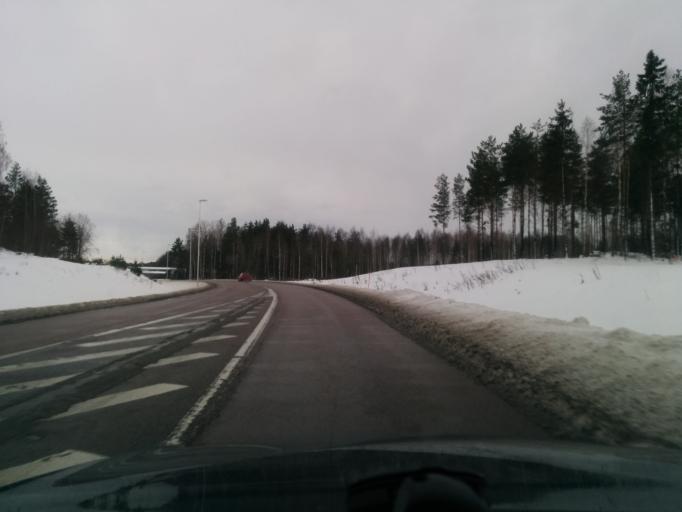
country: SE
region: Vaestmanland
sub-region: Vasteras
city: Vasteras
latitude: 59.5959
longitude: 16.4371
